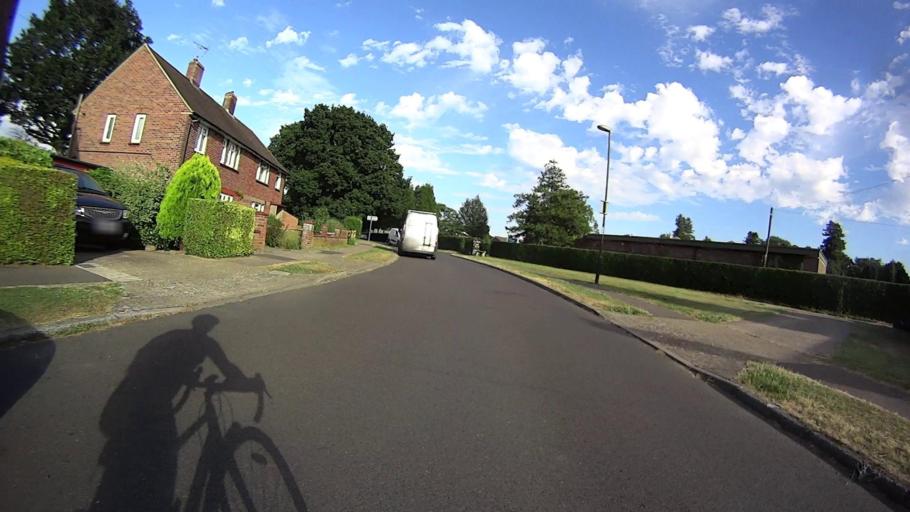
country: GB
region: England
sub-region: West Sussex
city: Gossops Green
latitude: 51.1168
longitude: -0.2058
